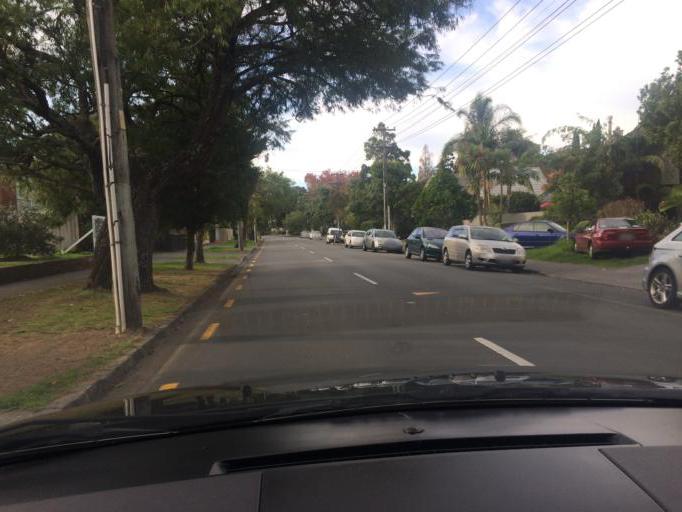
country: NZ
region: Auckland
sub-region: Auckland
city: Auckland
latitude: -36.8712
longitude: 174.7955
